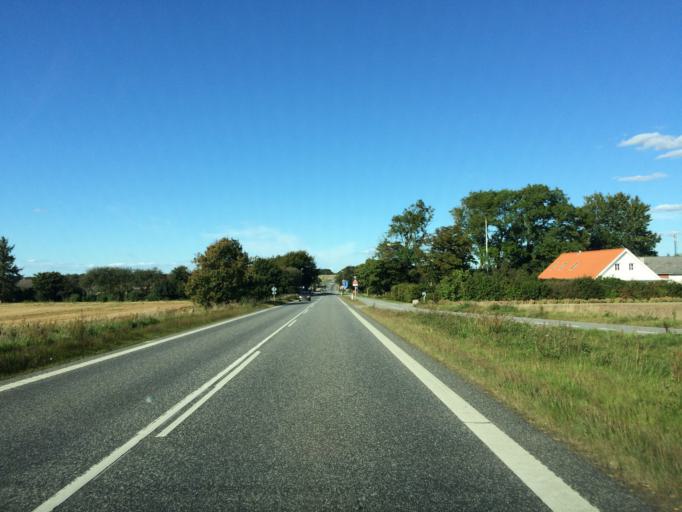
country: DK
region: Central Jutland
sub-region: Holstebro Kommune
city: Holstebro
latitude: 56.3119
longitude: 8.6051
